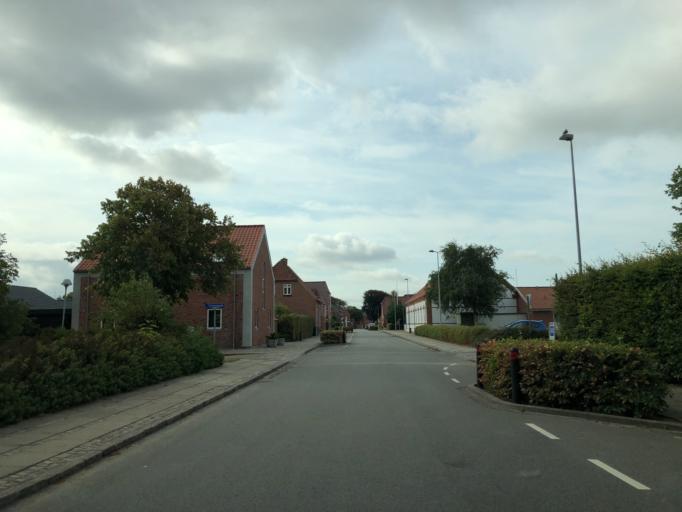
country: DK
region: Central Jutland
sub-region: Ringkobing-Skjern Kommune
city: Skjern
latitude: 55.9512
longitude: 8.4936
